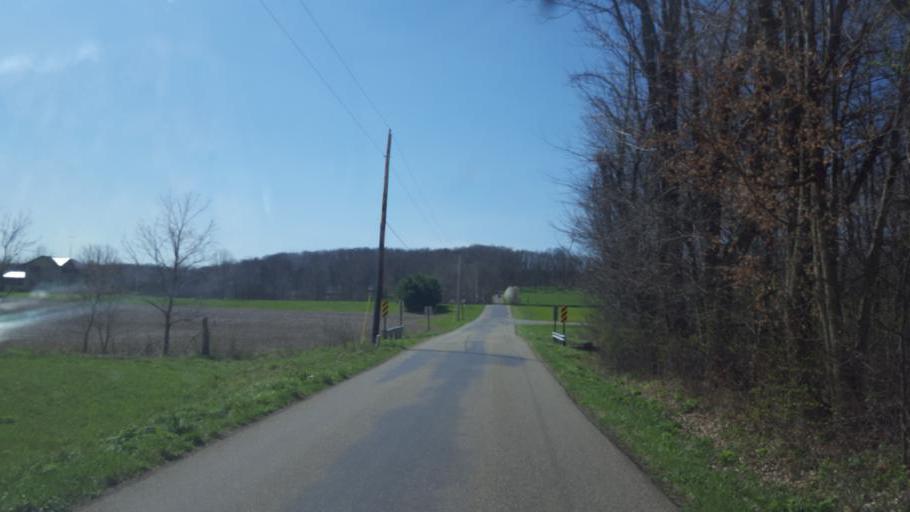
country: US
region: Ohio
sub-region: Knox County
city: Gambier
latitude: 40.3724
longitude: -82.4059
